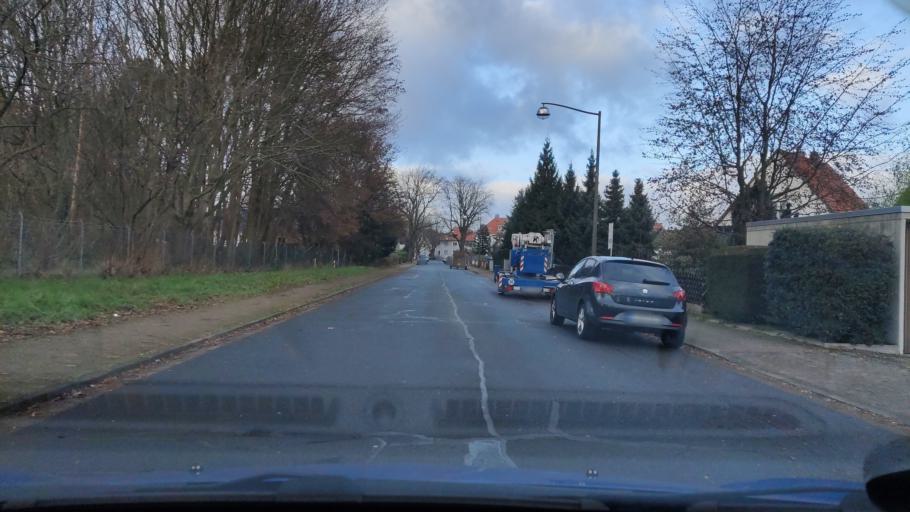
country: DE
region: Lower Saxony
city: Langenhagen
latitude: 52.4474
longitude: 9.7289
